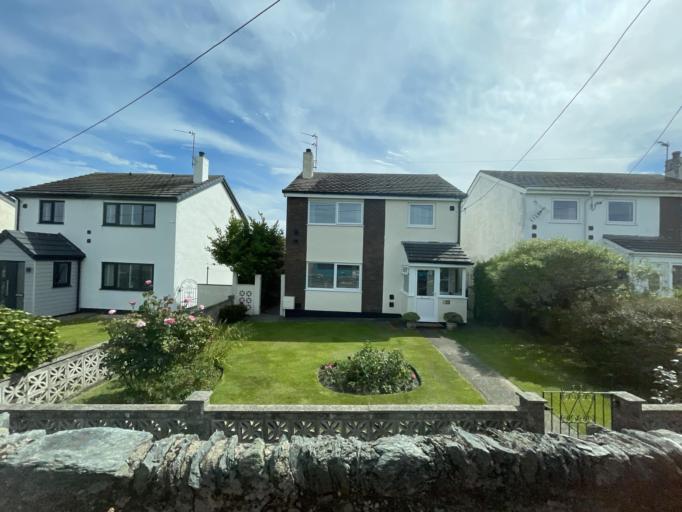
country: GB
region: Wales
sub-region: Anglesey
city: Valley
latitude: 53.2769
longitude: -4.5428
